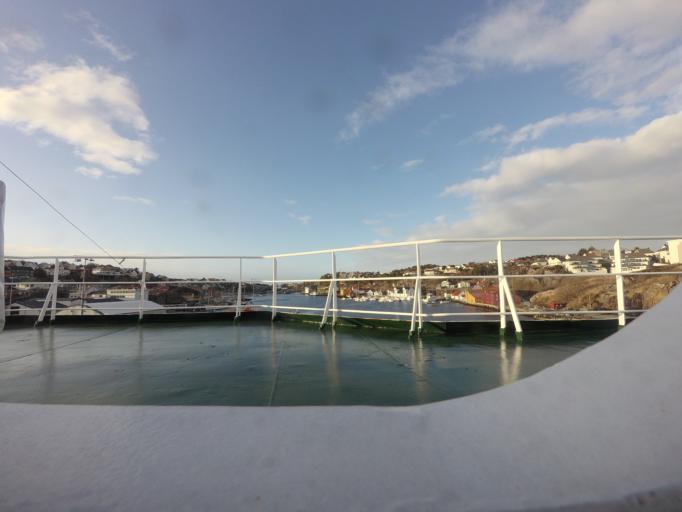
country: NO
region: More og Romsdal
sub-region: Kristiansund
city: Kristiansund
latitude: 63.1149
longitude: 7.7371
